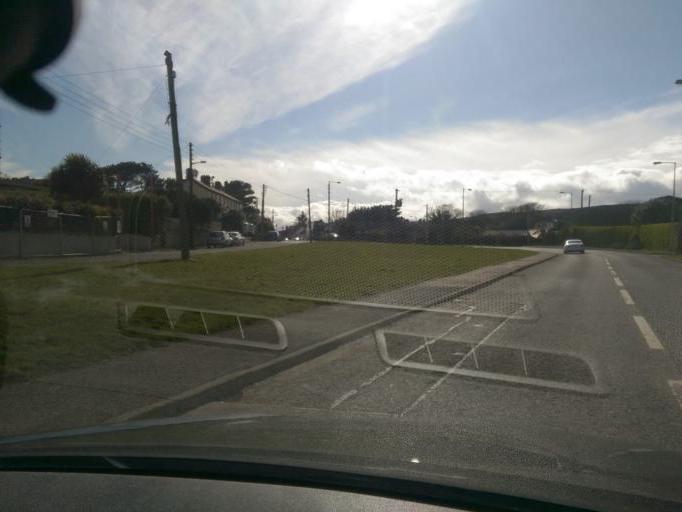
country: IE
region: Leinster
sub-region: Fingal County
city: Howth
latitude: 53.3735
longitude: -6.0571
